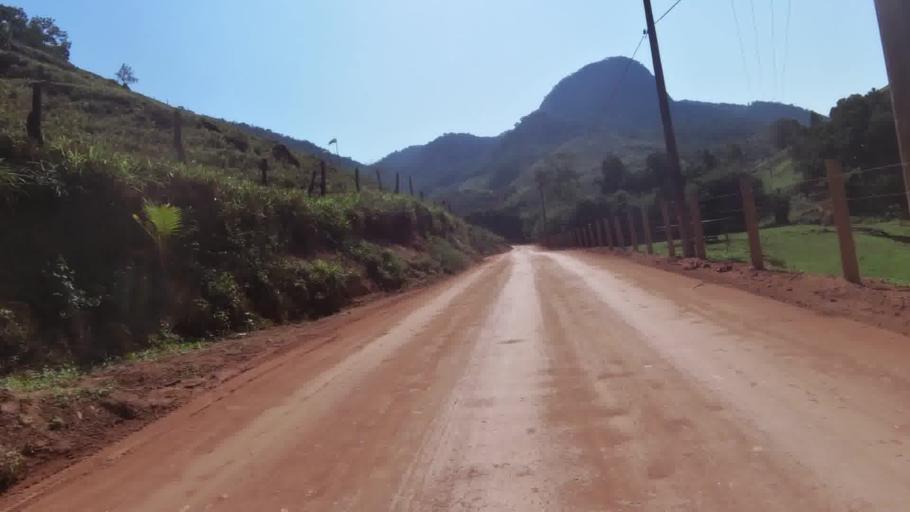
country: BR
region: Espirito Santo
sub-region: Alfredo Chaves
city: Alfredo Chaves
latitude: -20.6340
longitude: -40.7656
